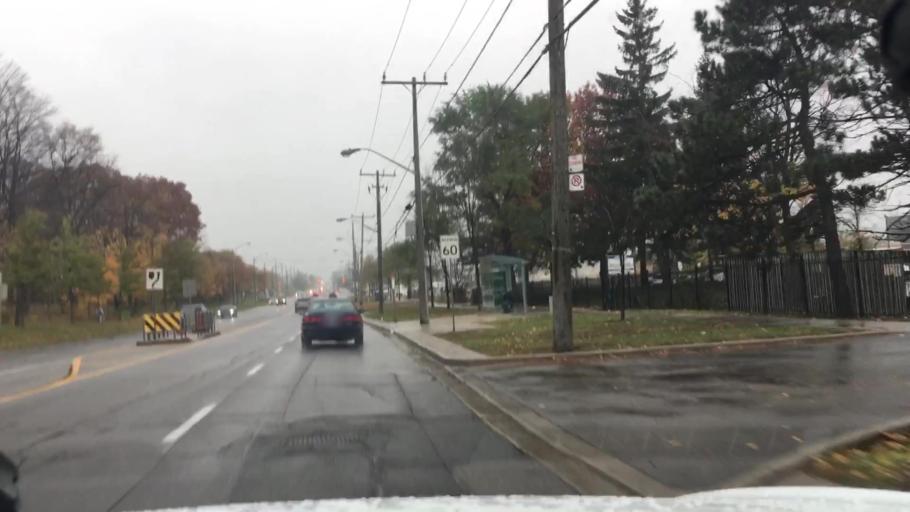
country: CA
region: Ontario
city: Concord
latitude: 43.7480
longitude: -79.4873
